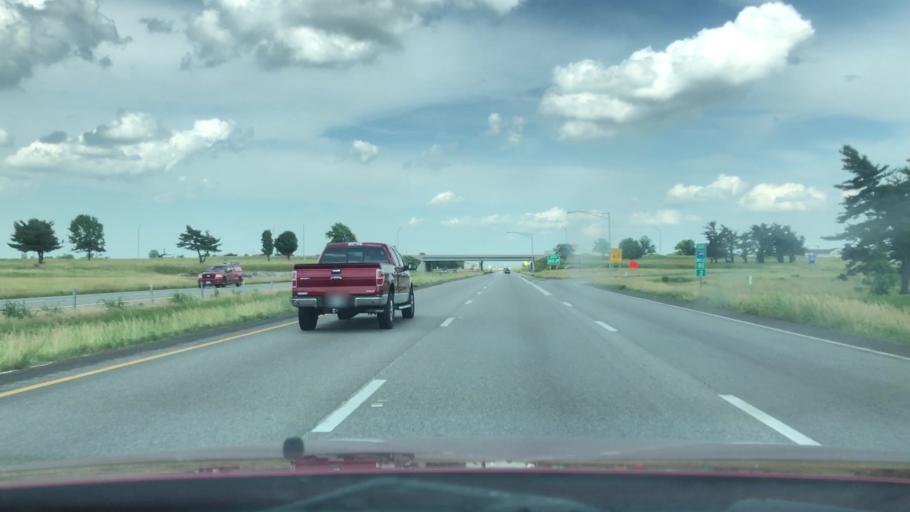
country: US
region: Missouri
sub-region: Greene County
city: Springfield
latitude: 37.2501
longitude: -93.2667
